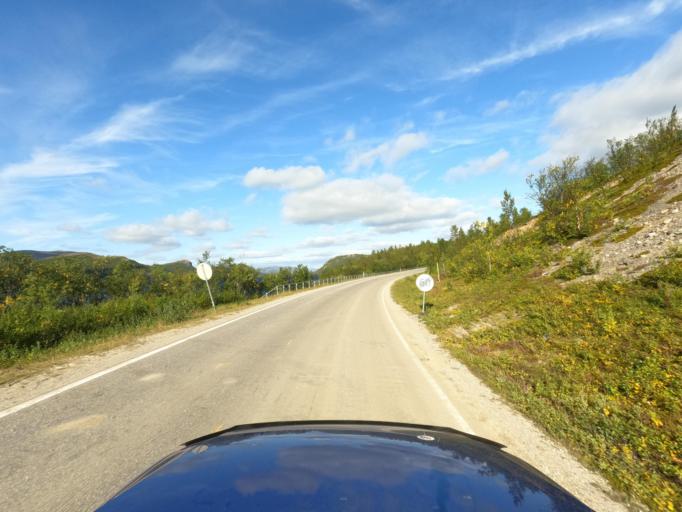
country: NO
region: Finnmark Fylke
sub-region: Porsanger
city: Lakselv
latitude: 69.8948
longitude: 24.9915
